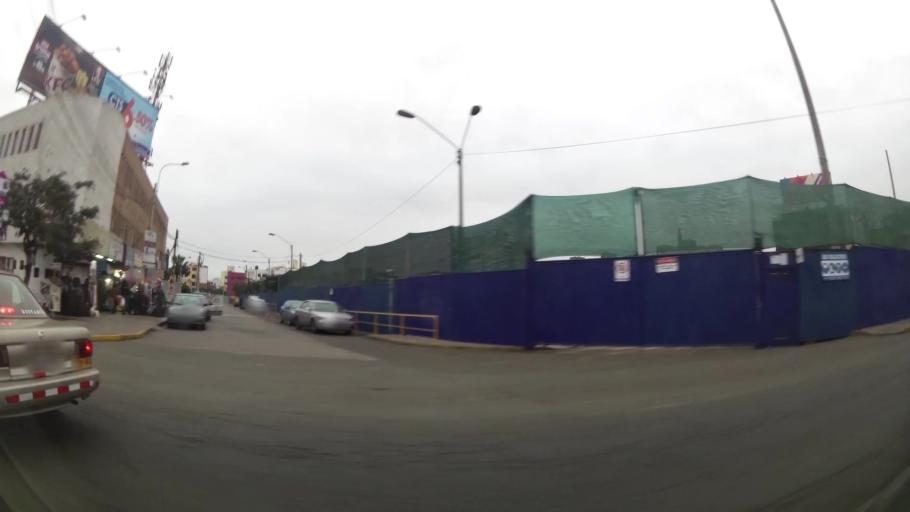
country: PE
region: Lima
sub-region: Lima
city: San Isidro
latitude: -12.0763
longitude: -77.0641
